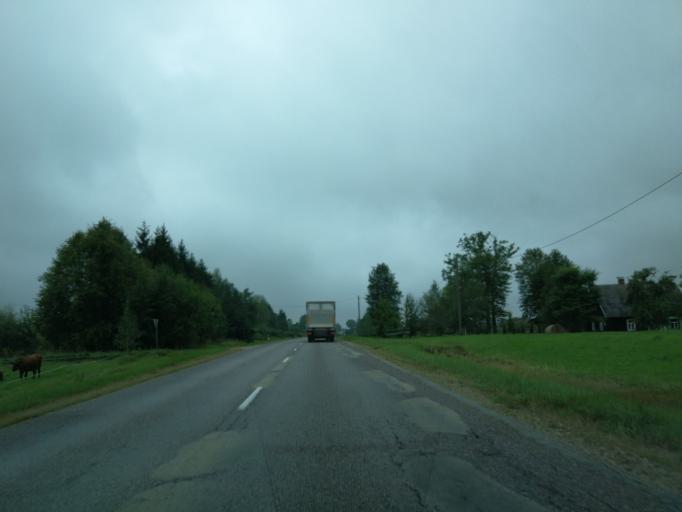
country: LV
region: Livani
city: Livani
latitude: 56.3474
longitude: 26.3002
